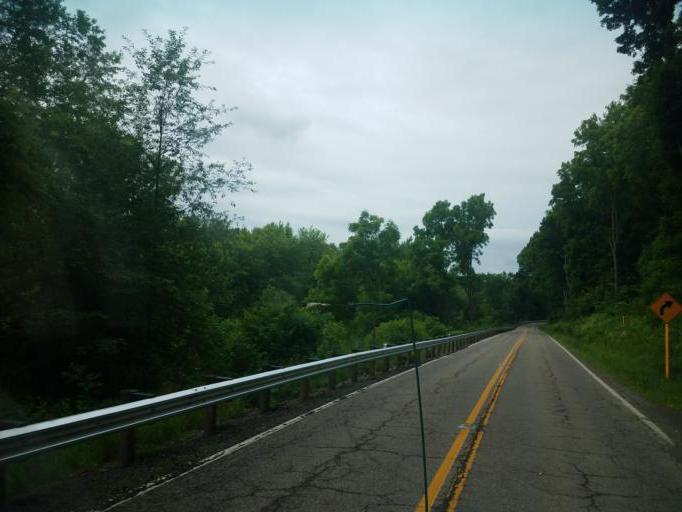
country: US
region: Ohio
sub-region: Columbiana County
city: Leetonia
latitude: 40.8486
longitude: -80.8050
